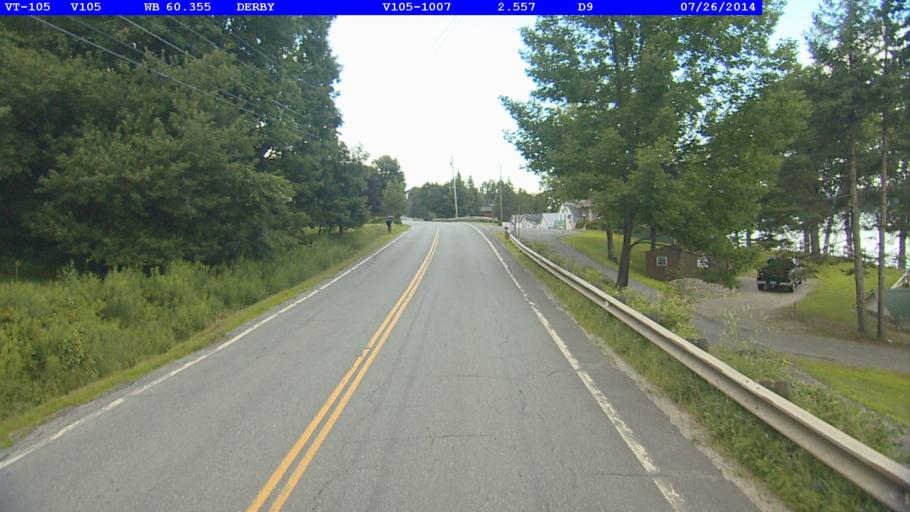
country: US
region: Vermont
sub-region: Orleans County
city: Newport
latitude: 44.9250
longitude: -72.1105
